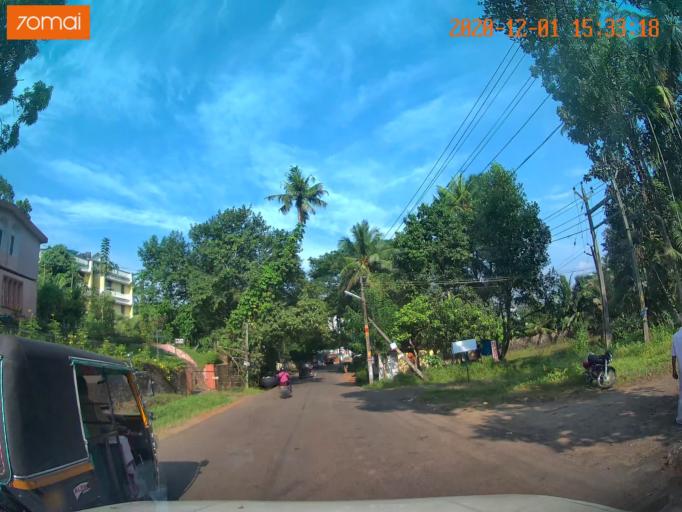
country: IN
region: Kerala
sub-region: Ernakulam
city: Muvattupuzha
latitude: 9.9763
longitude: 76.5772
